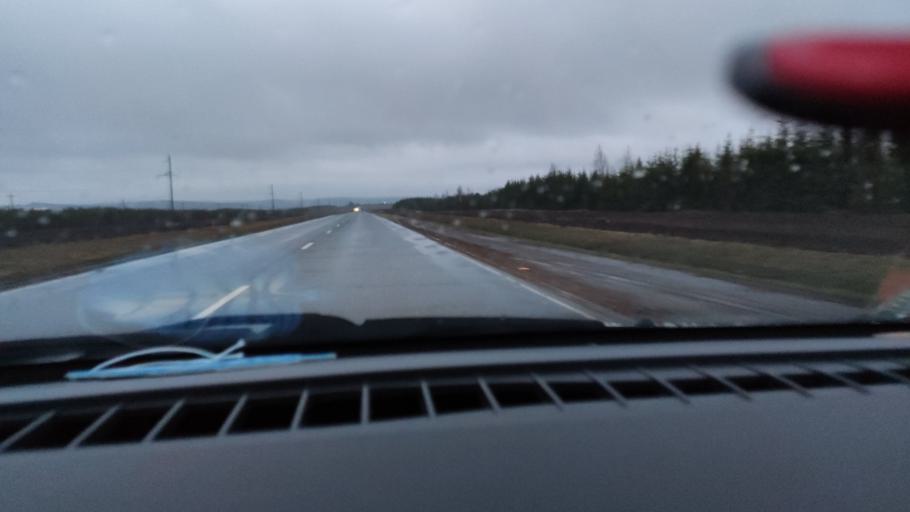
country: RU
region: Udmurtiya
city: Alnashi
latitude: 56.2124
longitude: 52.4335
